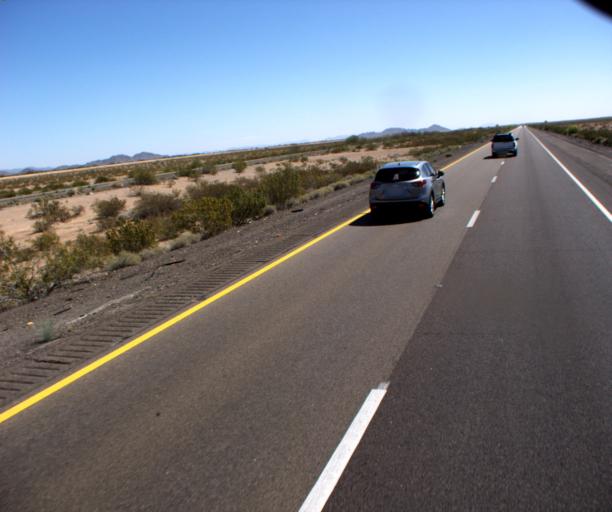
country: US
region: Arizona
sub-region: La Paz County
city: Salome
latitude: 33.6042
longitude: -113.5888
